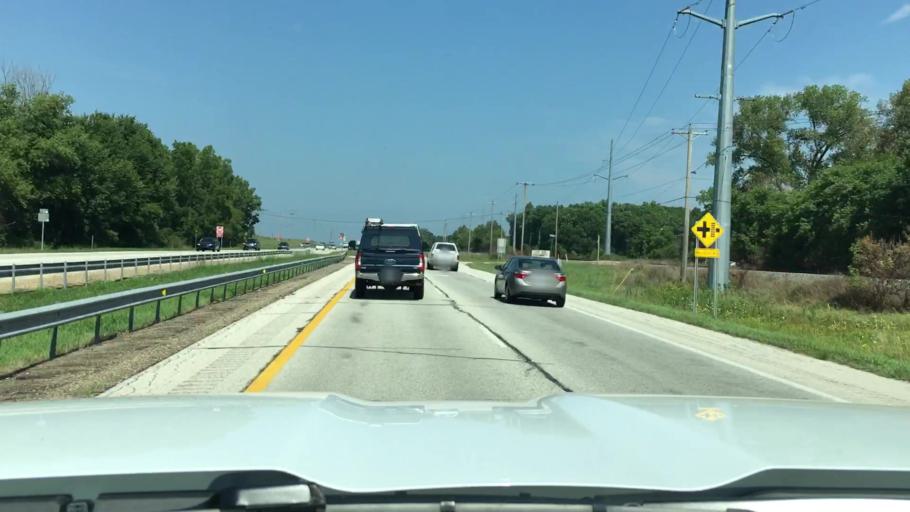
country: US
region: Michigan
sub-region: Kalamazoo County
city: Schoolcraft
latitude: 42.0615
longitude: -85.6360
